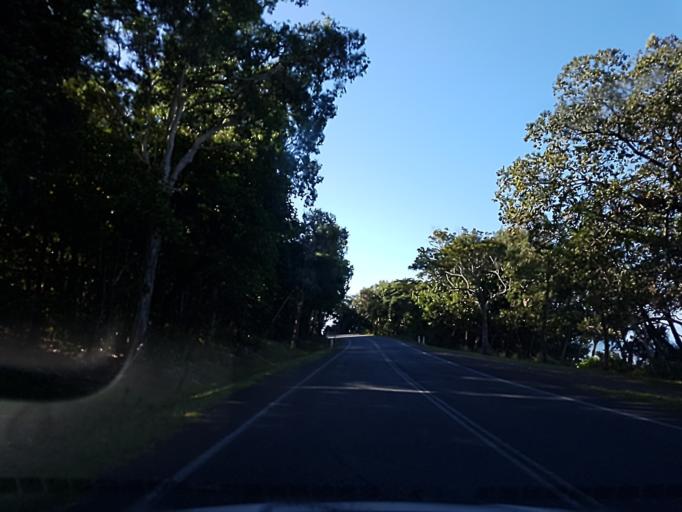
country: AU
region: Queensland
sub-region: Cairns
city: Port Douglas
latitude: -16.3684
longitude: 145.4120
